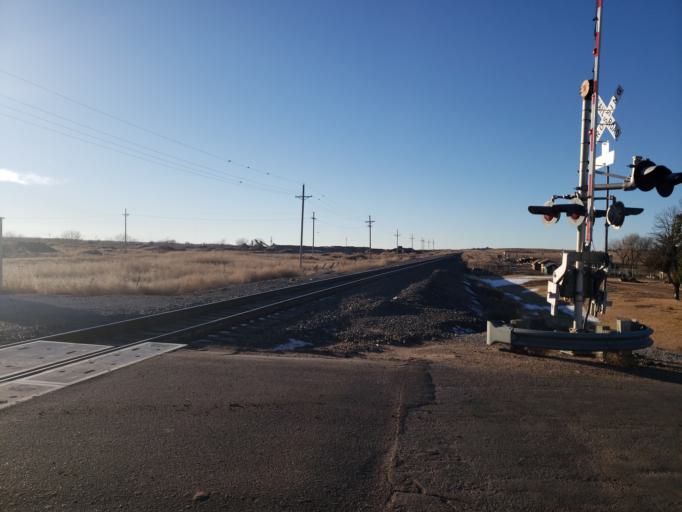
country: US
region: Kansas
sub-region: Ford County
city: Dodge City
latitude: 37.7825
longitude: -100.1792
